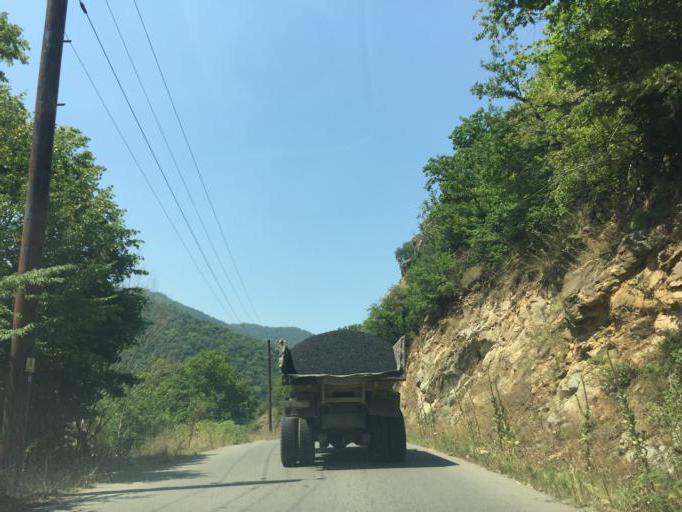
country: AZ
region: Kalbacar Rayonu
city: Kerbakhiar
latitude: 40.1234
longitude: 46.4241
